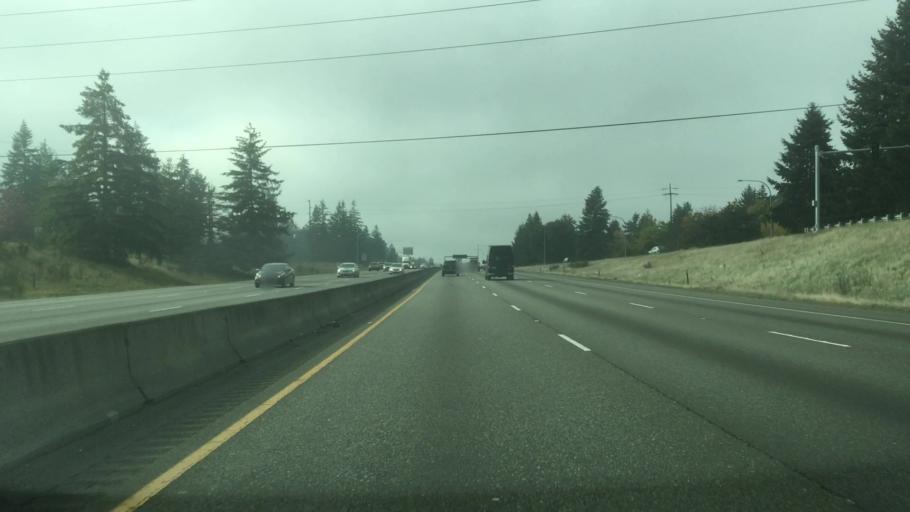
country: US
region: Washington
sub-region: Pierce County
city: DuPont
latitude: 47.0926
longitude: -122.6253
